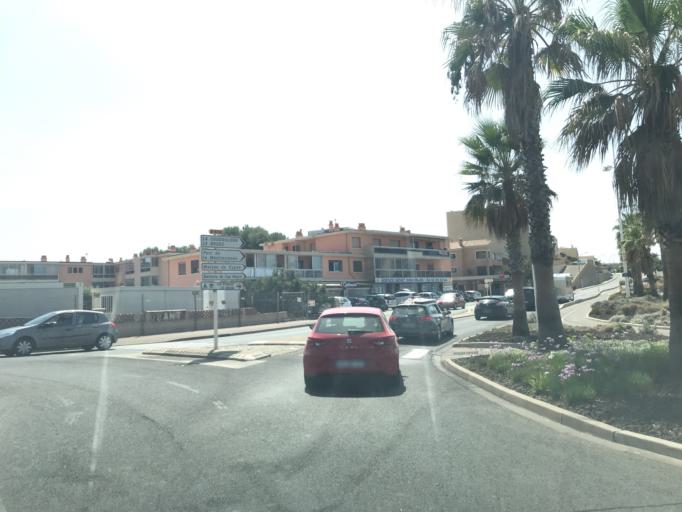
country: FR
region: Provence-Alpes-Cote d'Azur
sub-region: Departement du Var
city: Sanary-sur-Mer
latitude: 43.1068
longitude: 5.8141
